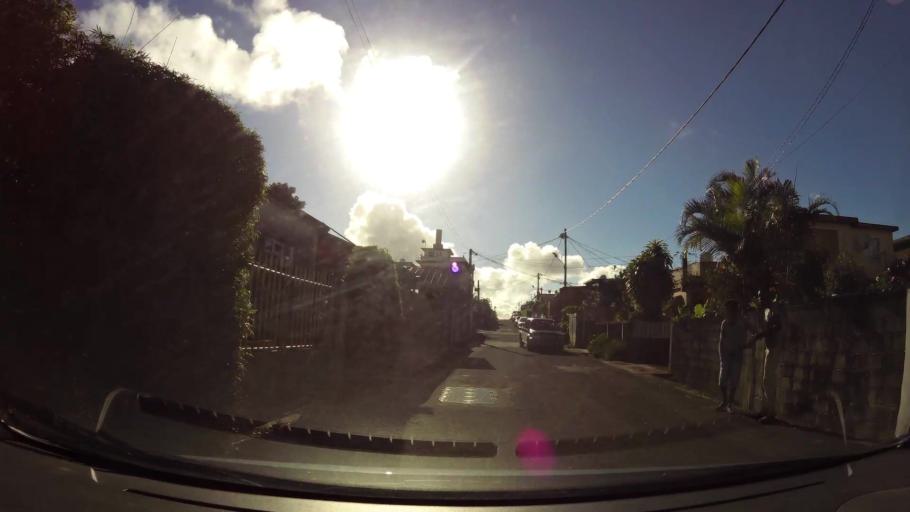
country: MU
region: Plaines Wilhems
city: Curepipe
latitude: -20.3183
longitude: 57.5363
